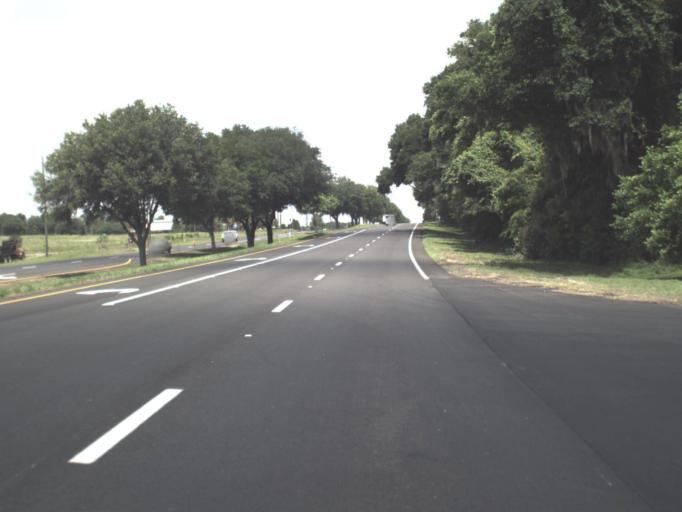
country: US
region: Florida
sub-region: Alachua County
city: Alachua
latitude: 29.7775
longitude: -82.4477
